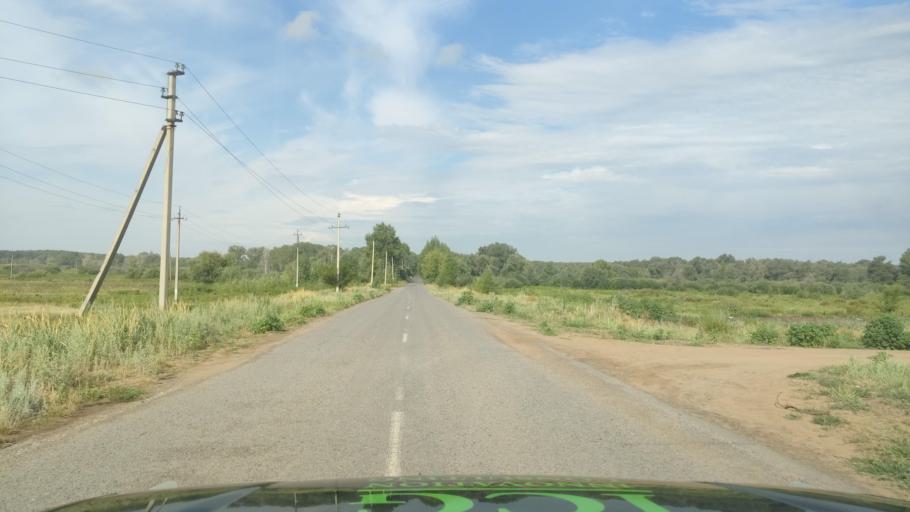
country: KZ
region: Pavlodar
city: Leninskiy
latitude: 52.4773
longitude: 76.8159
